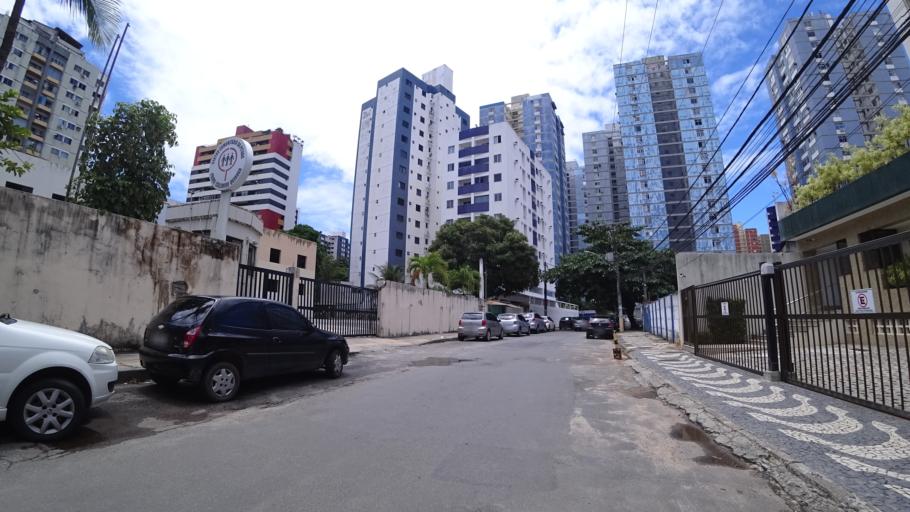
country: BR
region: Bahia
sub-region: Salvador
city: Salvador
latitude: -13.0018
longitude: -38.4603
